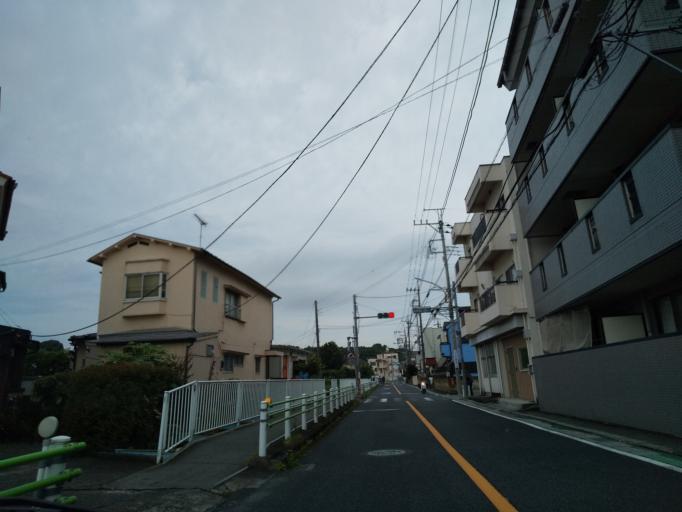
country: JP
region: Tokyo
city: Hino
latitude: 35.6825
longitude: 139.3883
